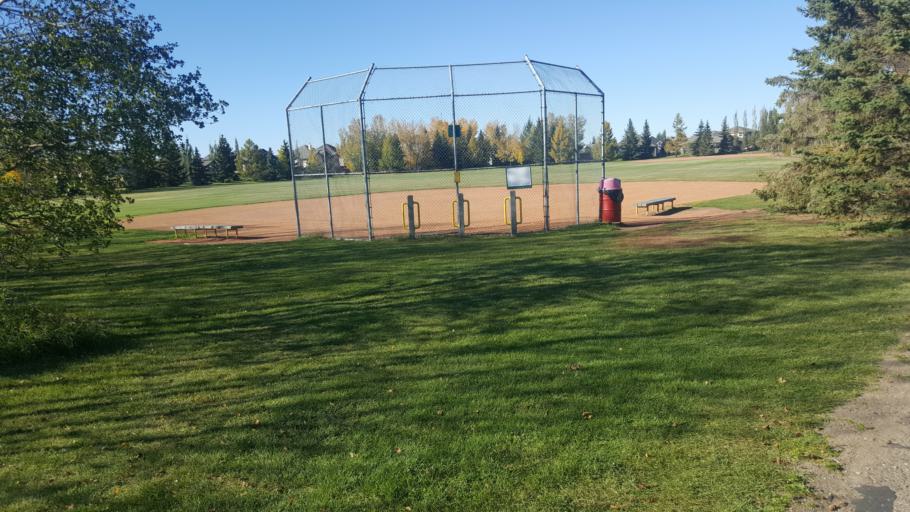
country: CA
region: Saskatchewan
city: Lloydminster
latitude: 53.2638
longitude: -110.0369
